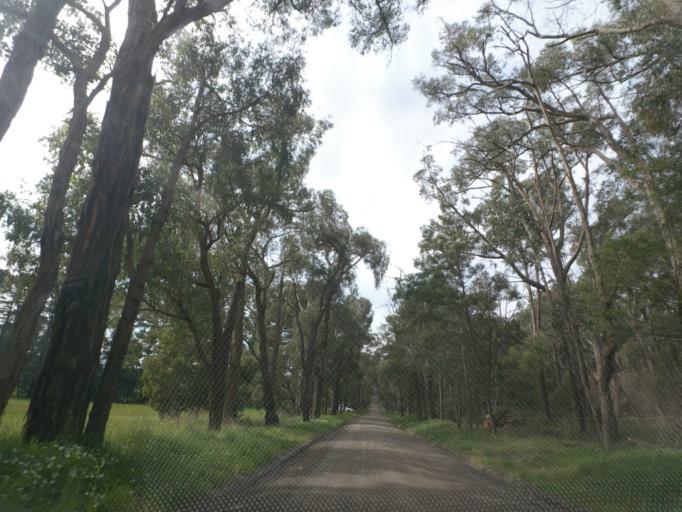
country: AU
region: Victoria
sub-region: Knox
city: The Basin
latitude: -37.8389
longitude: 145.3299
